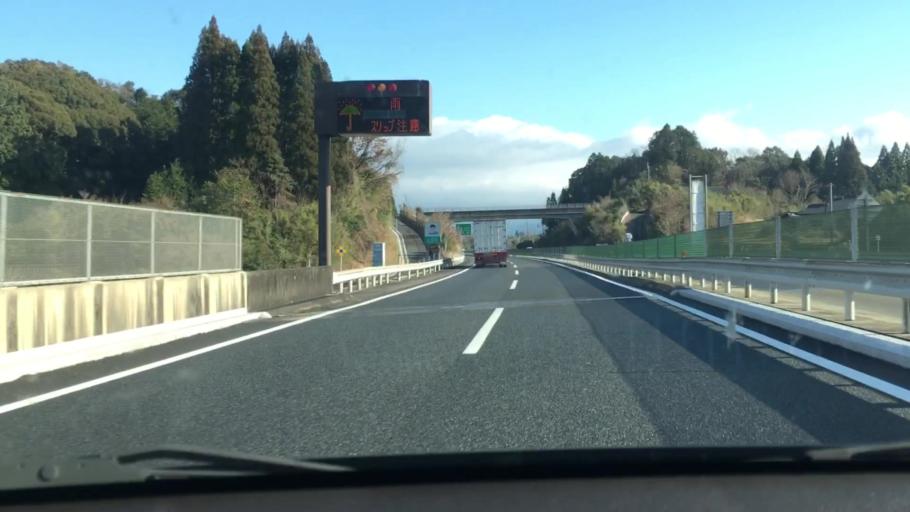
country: JP
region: Kumamoto
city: Hitoyoshi
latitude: 32.2347
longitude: 130.7656
